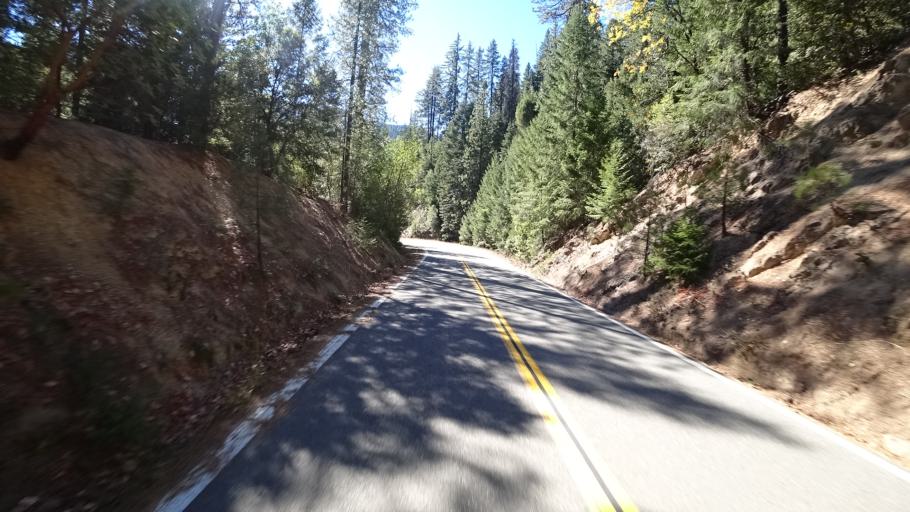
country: US
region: California
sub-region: Trinity County
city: Weaverville
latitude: 41.2260
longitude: -123.0177
